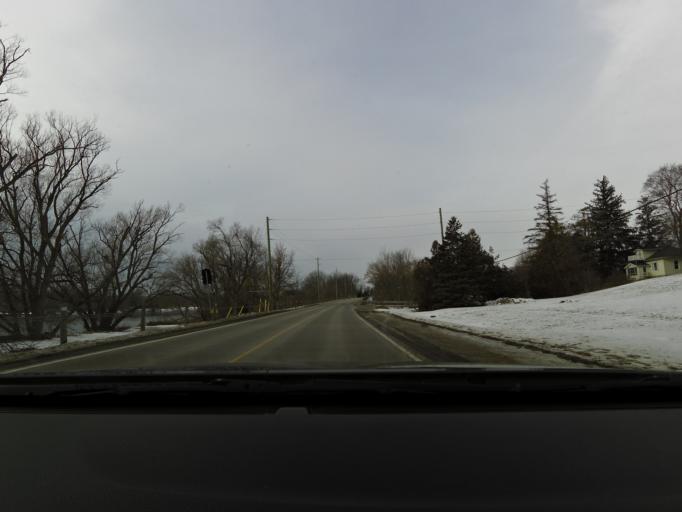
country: CA
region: Ontario
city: Ancaster
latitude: 43.0649
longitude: -79.9327
